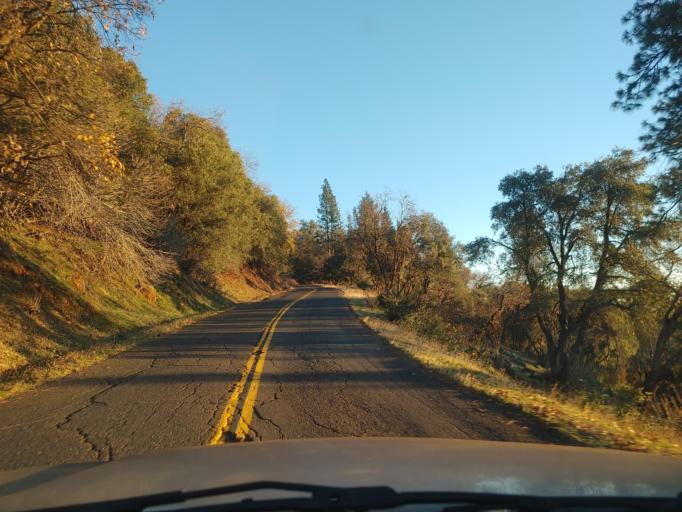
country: US
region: California
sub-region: Tuolumne County
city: Cedar Ridge
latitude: 38.0396
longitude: -120.3113
